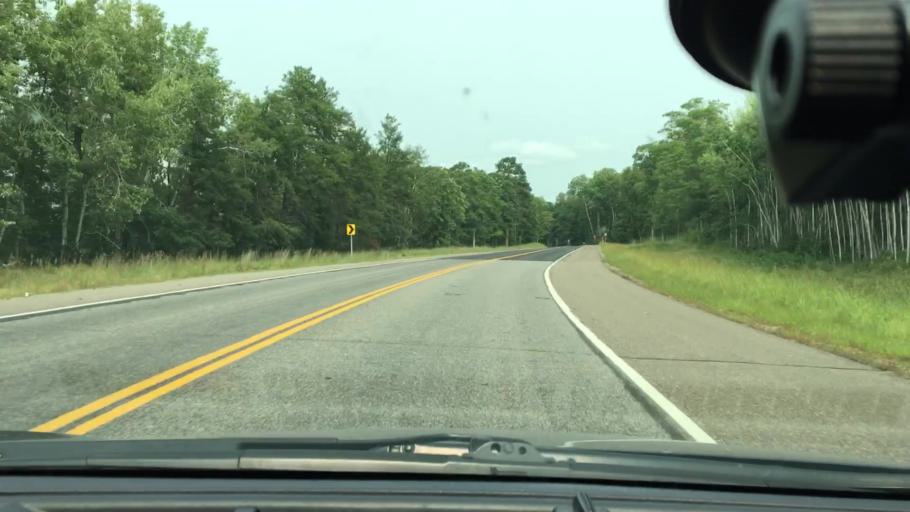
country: US
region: Minnesota
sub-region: Crow Wing County
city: Cross Lake
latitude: 46.7003
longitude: -94.0642
